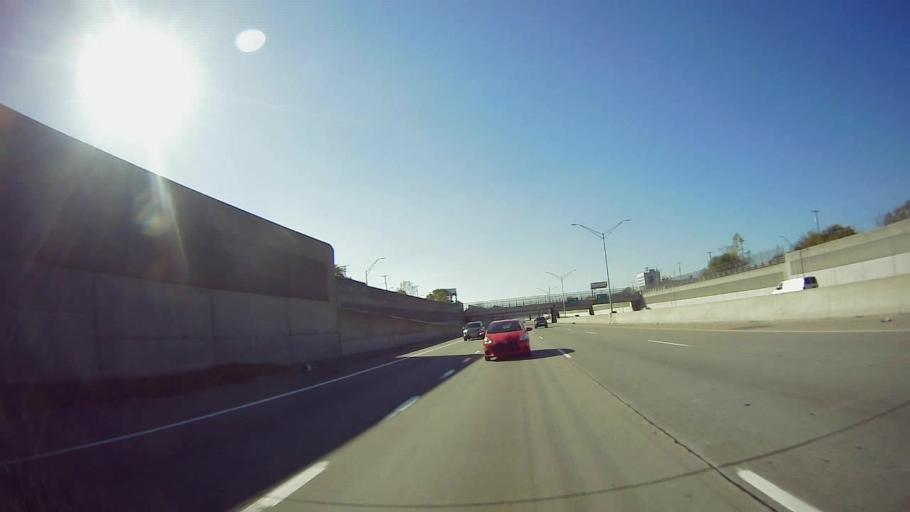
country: US
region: Michigan
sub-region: Wayne County
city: Highland Park
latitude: 42.4050
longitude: -83.0909
